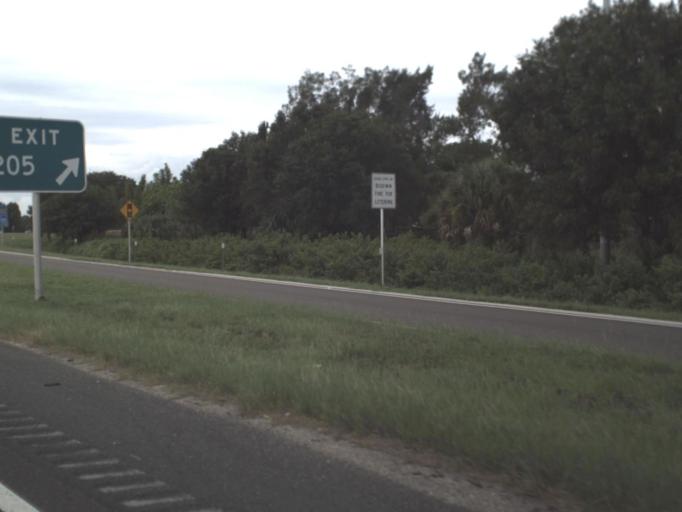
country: US
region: Florida
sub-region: Sarasota County
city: Lake Sarasota
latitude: 27.2733
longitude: -82.4491
